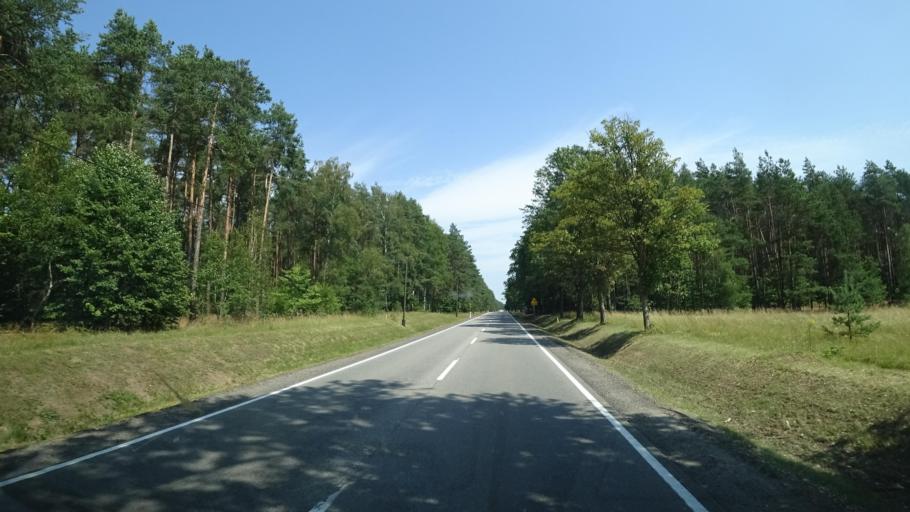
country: PL
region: Pomeranian Voivodeship
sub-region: Powiat koscierski
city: Koscierzyna
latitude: 54.1673
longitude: 18.0483
